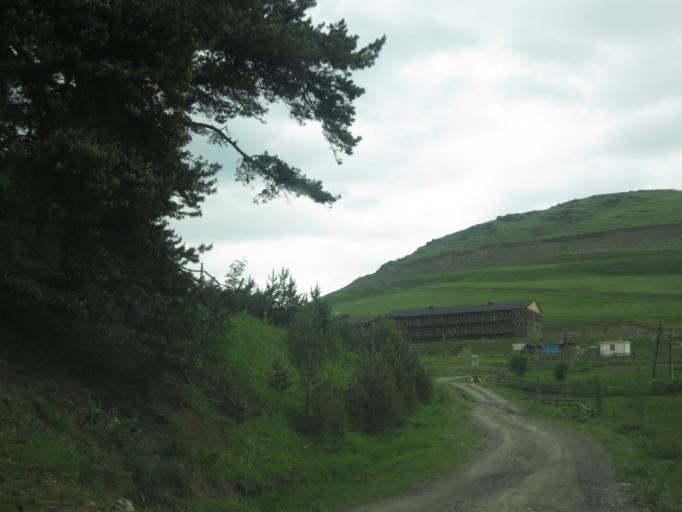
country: RU
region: Chechnya
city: Itum-Kali
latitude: 42.3733
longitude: 45.6297
